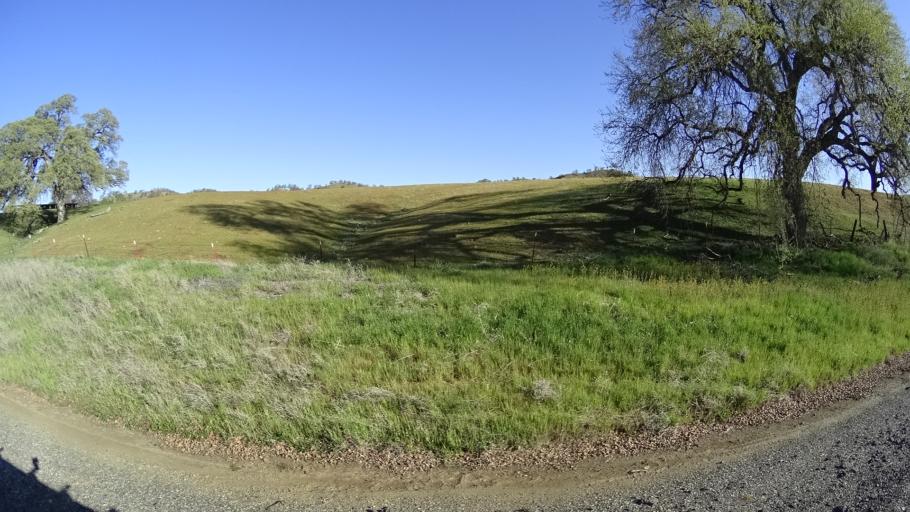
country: US
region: California
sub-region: Tehama County
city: Rancho Tehama Reserve
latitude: 39.7885
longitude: -122.4931
